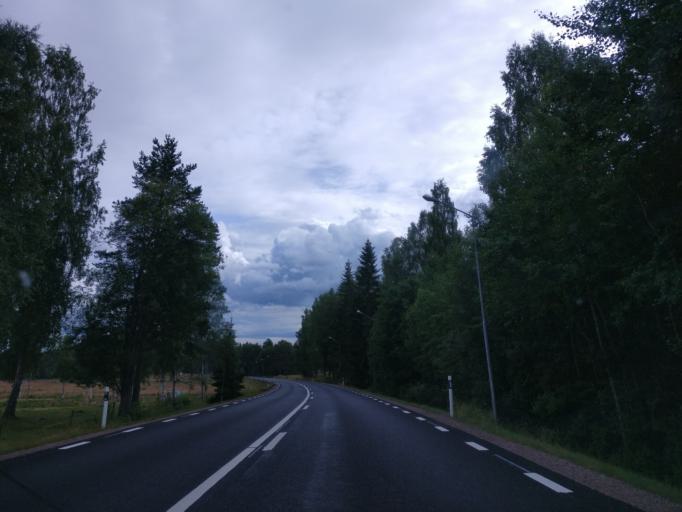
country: SE
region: Vaermland
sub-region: Hagfors Kommun
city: Ekshaerad
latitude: 60.0679
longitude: 13.5492
